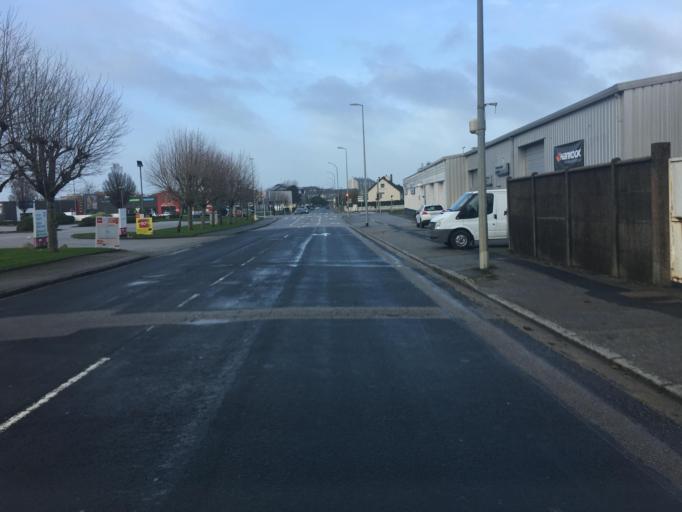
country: FR
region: Lower Normandy
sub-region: Departement de la Manche
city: Cherbourg-Octeville
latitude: 49.6336
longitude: -1.6013
